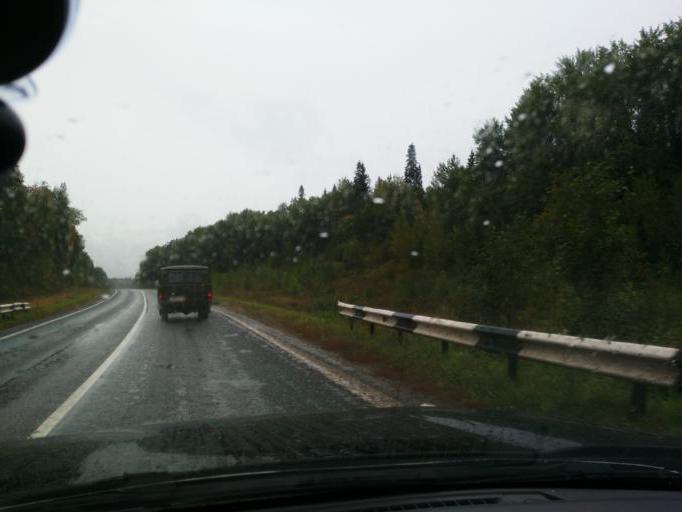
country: RU
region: Perm
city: Yugo-Kamskiy
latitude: 57.6302
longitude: 55.6162
